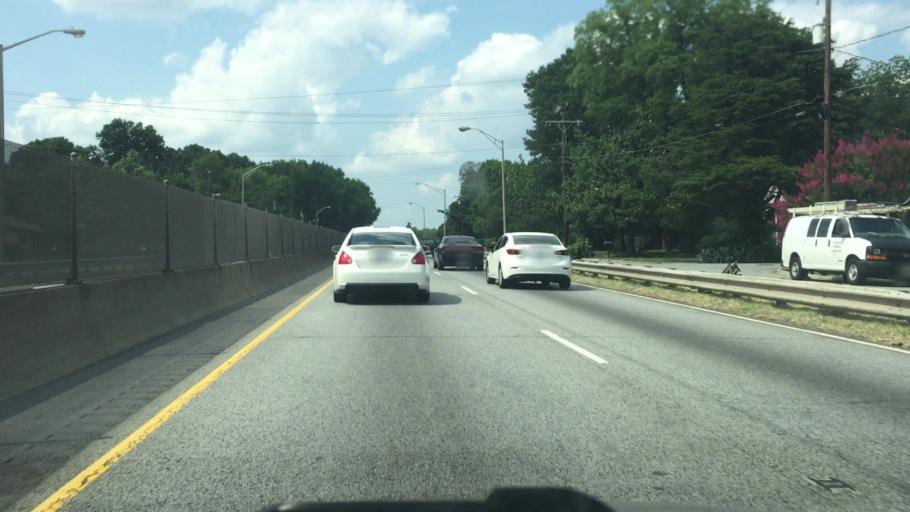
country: US
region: North Carolina
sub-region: Guilford County
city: Greensboro
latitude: 36.0953
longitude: -79.7656
